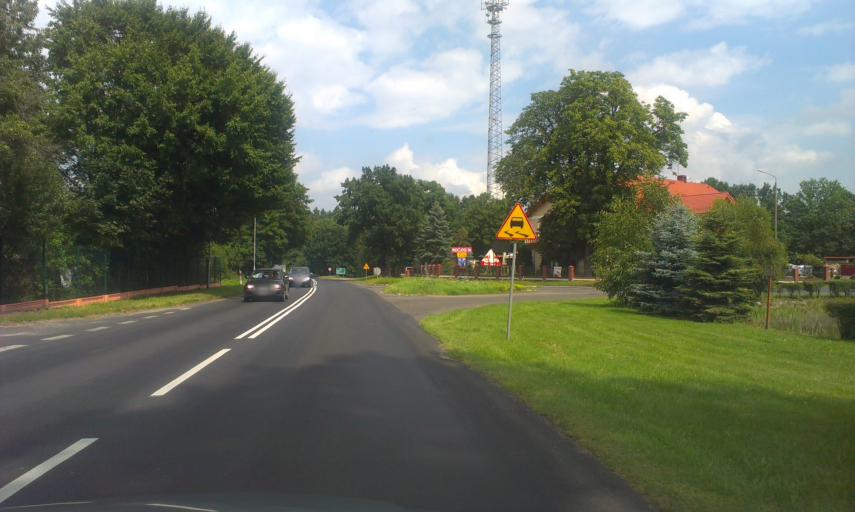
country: PL
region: West Pomeranian Voivodeship
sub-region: Powiat bialogardzki
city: Bialogard
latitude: 53.9469
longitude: 16.0606
